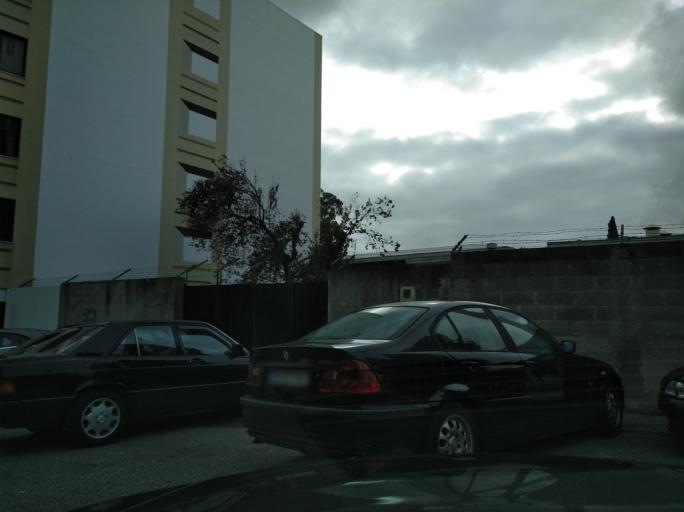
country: PT
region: Lisbon
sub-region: Odivelas
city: Olival do Basto
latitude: 38.7615
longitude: -9.1395
